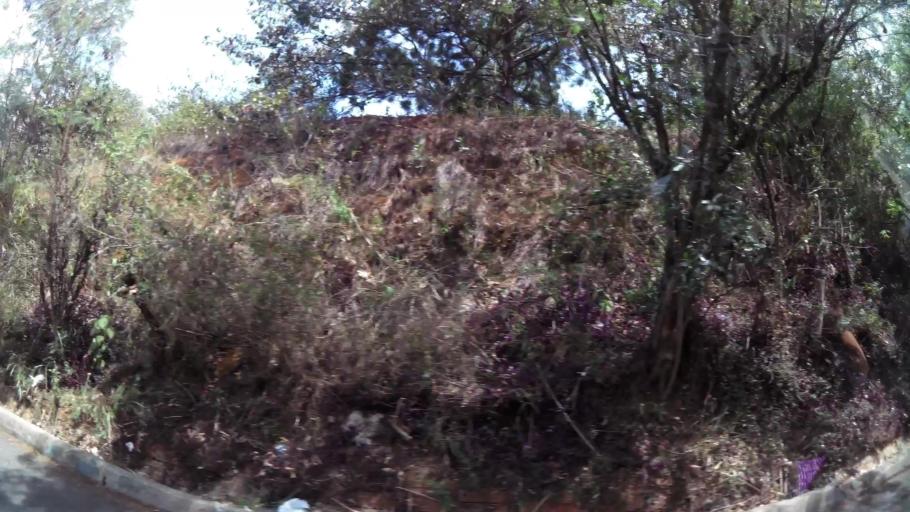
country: CO
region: Antioquia
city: Bello
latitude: 6.3486
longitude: -75.5460
